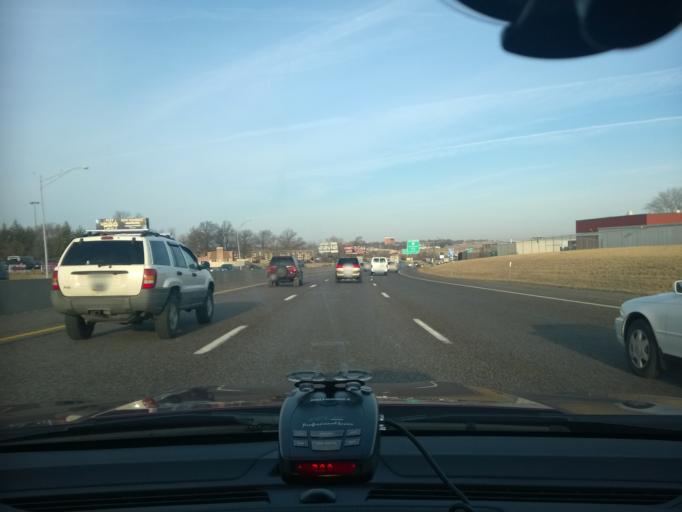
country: US
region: Missouri
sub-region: Saint Louis County
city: Saint Ann
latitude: 38.7403
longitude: -90.3723
